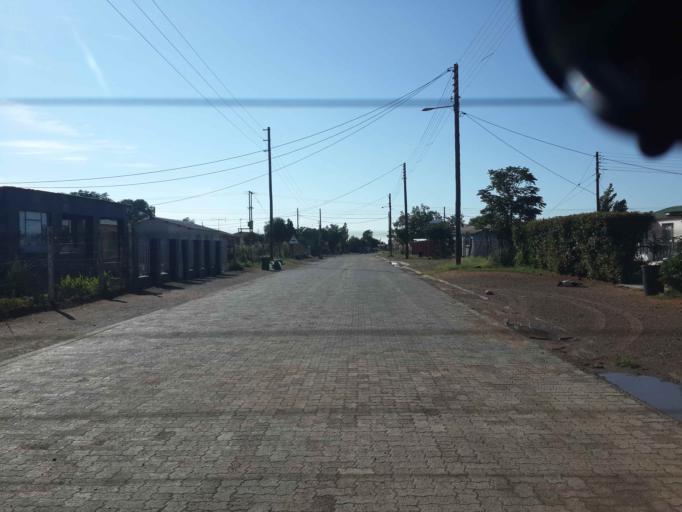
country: ZA
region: Northern Cape
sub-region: Siyanda District Municipality
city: Danielskuil
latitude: -28.1953
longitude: 23.5324
